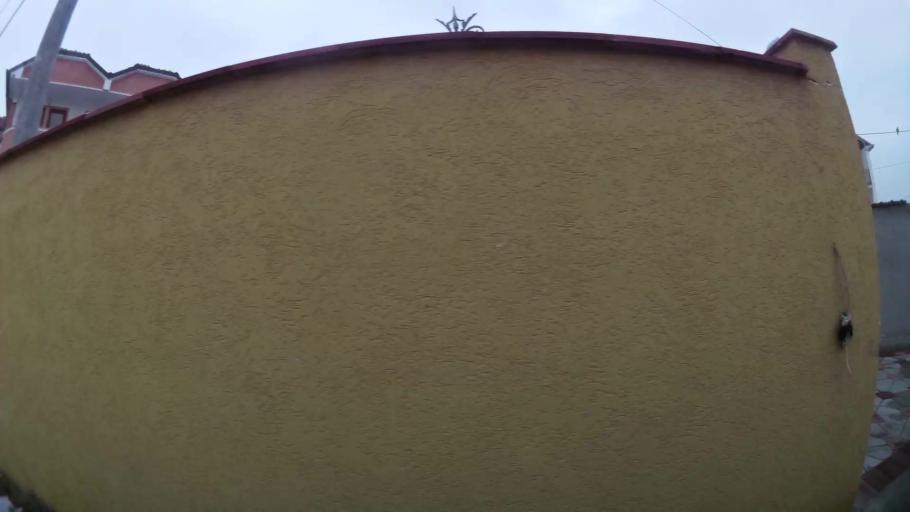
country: MK
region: Suto Orizari
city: Suto Orizare
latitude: 42.0412
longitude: 21.4286
